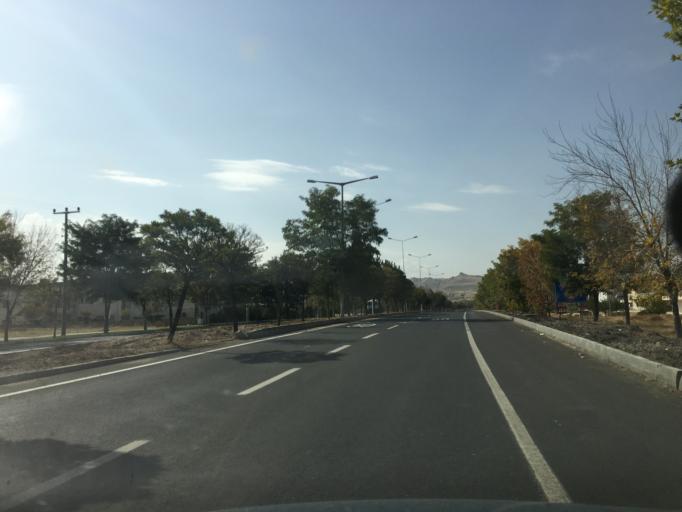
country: TR
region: Nevsehir
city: Avanos
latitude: 38.7048
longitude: 34.8545
